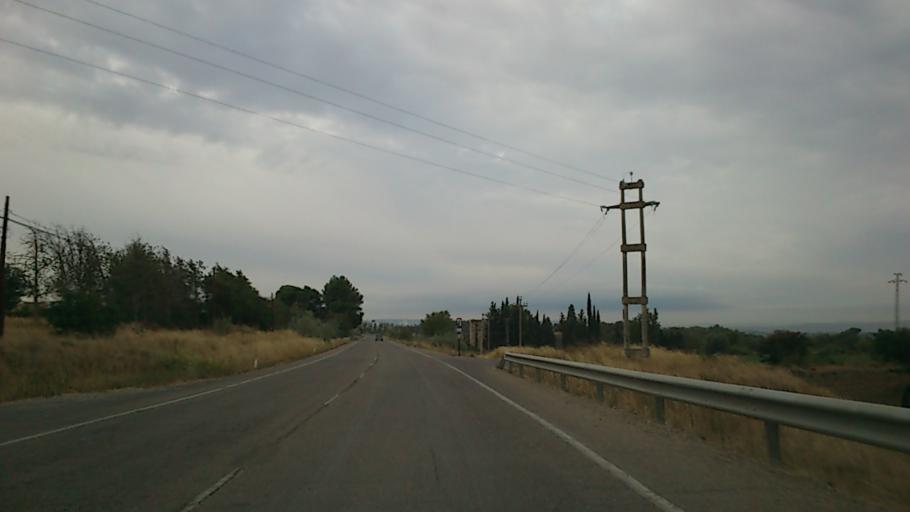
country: ES
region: Aragon
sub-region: Provincia de Zaragoza
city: Villanueva de Gallego
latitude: 41.7425
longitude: -0.8061
